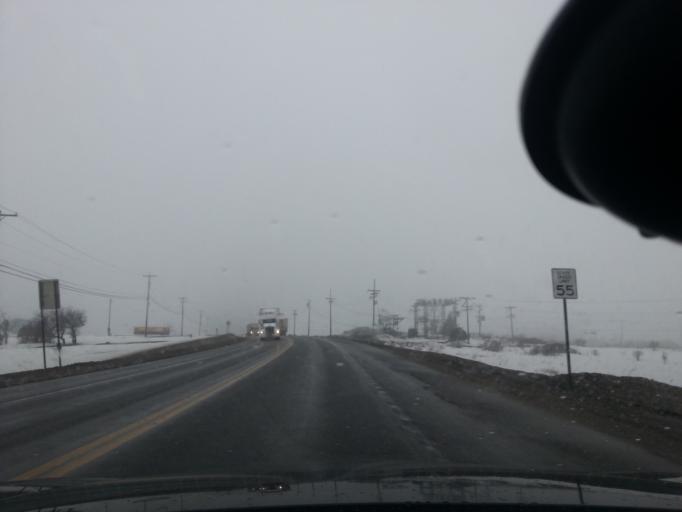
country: US
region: New York
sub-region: Jefferson County
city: Philadelphia
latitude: 44.1440
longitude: -75.7165
